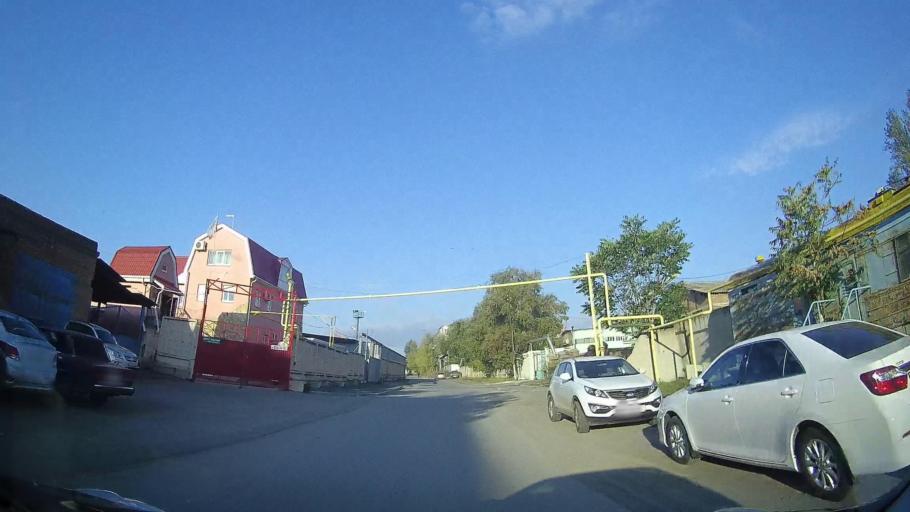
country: RU
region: Rostov
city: Severnyy
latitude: 47.2723
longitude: 39.6806
